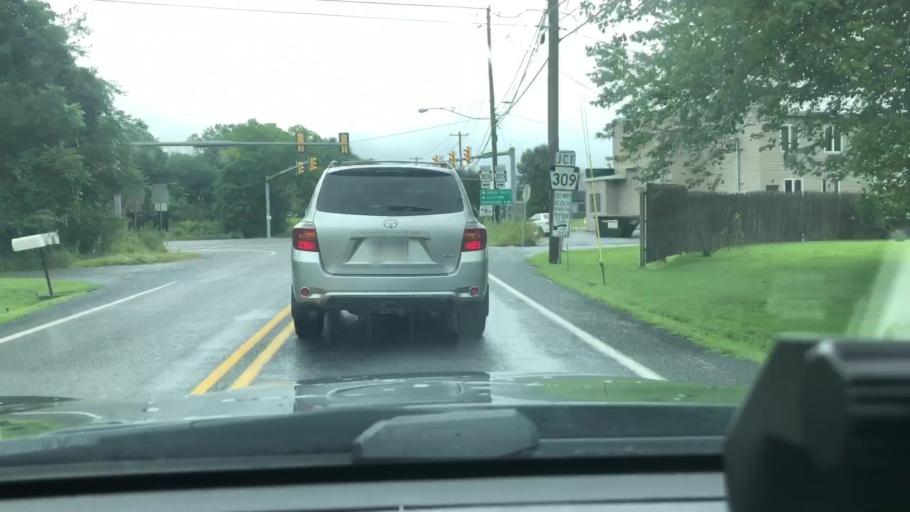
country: US
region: Pennsylvania
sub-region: Lehigh County
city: Coopersburg
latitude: 40.5232
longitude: -75.3889
